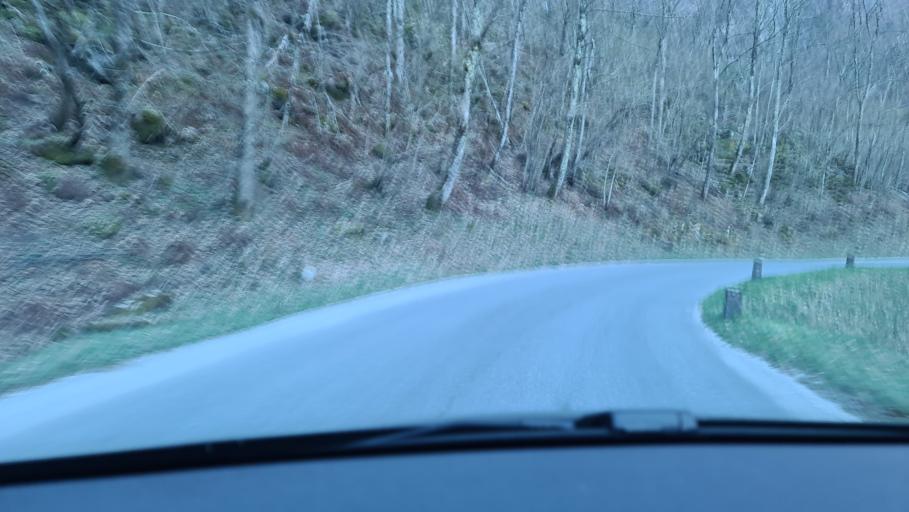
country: CH
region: Ticino
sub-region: Vallemaggia District
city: Cevio
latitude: 46.3766
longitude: 8.5478
